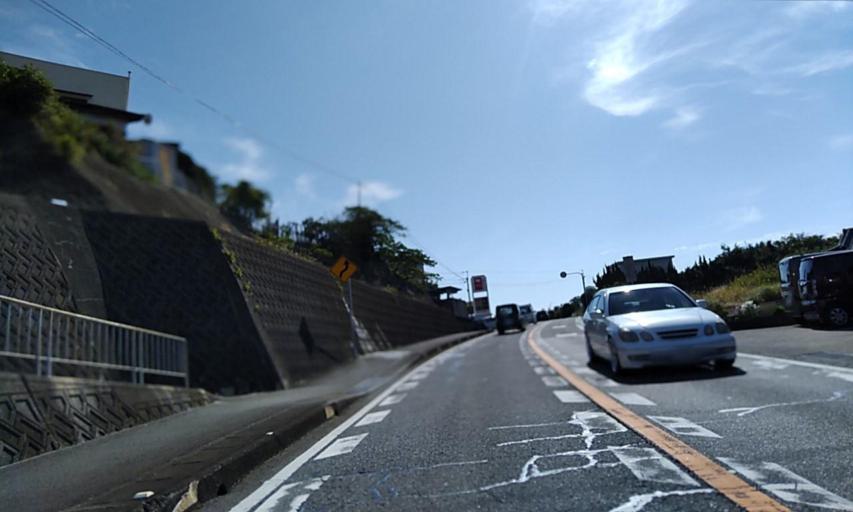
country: JP
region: Wakayama
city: Gobo
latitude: 33.8110
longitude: 135.2192
